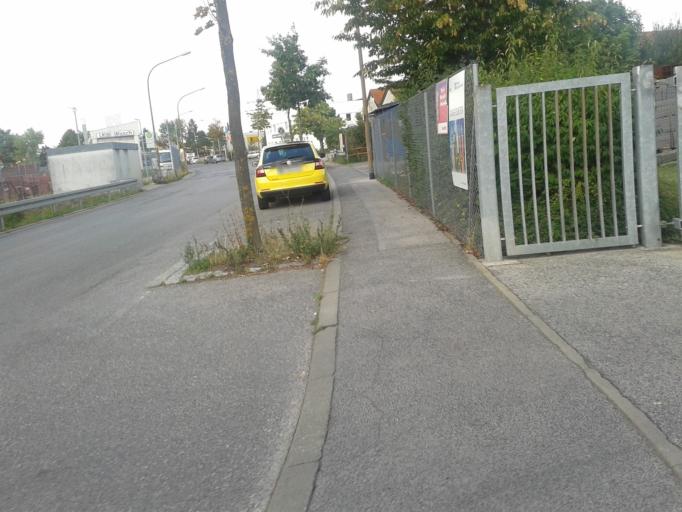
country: DE
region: Bavaria
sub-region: Upper Franconia
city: Bamberg
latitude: 49.9199
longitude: 10.9037
